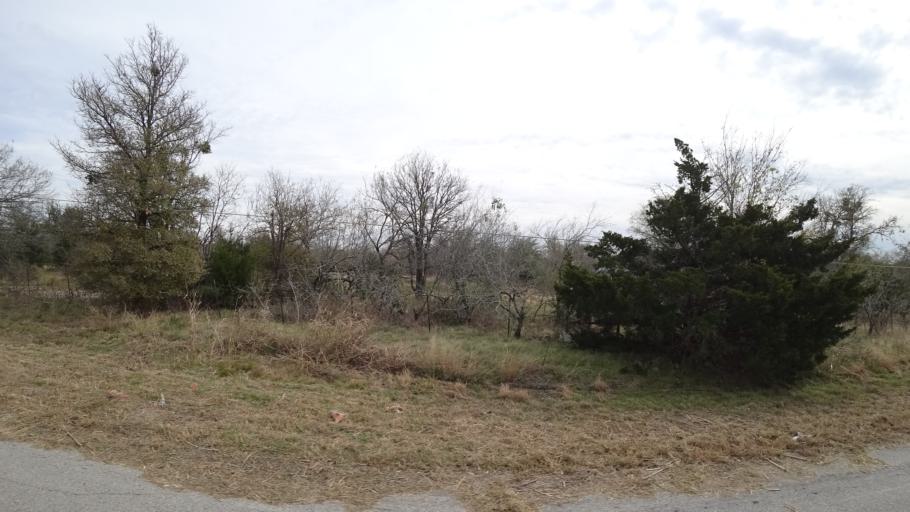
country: US
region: Texas
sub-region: Travis County
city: Garfield
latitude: 30.1367
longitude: -97.5914
